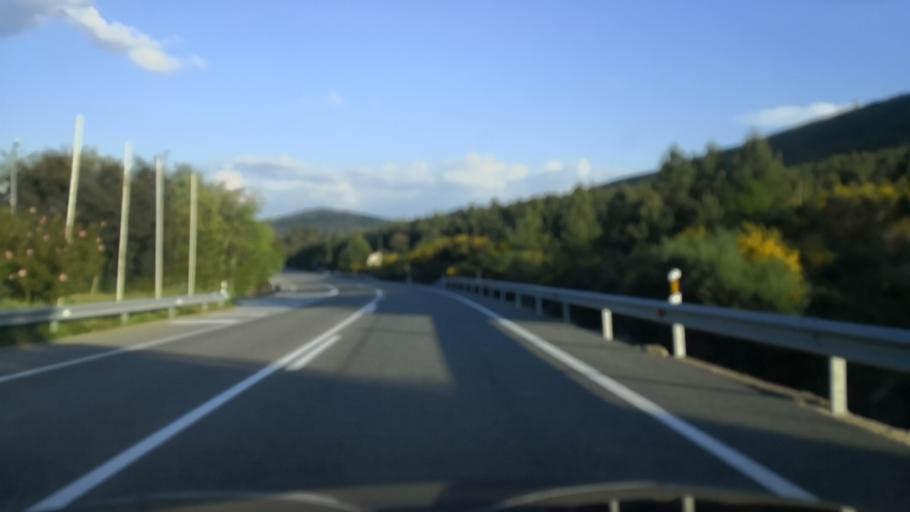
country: PT
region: Portalegre
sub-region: Portalegre
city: Sao Juliao
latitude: 39.3463
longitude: -7.2988
